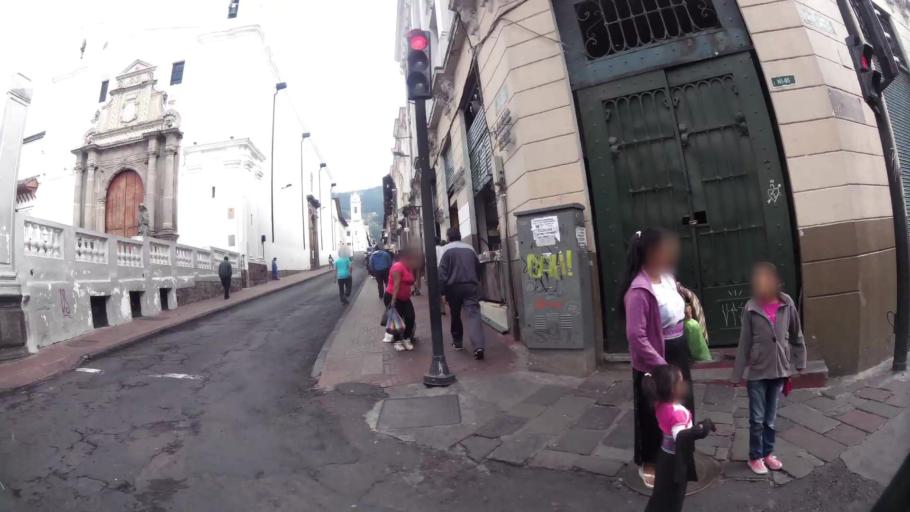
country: EC
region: Pichincha
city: Quito
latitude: -0.2226
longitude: -78.5150
